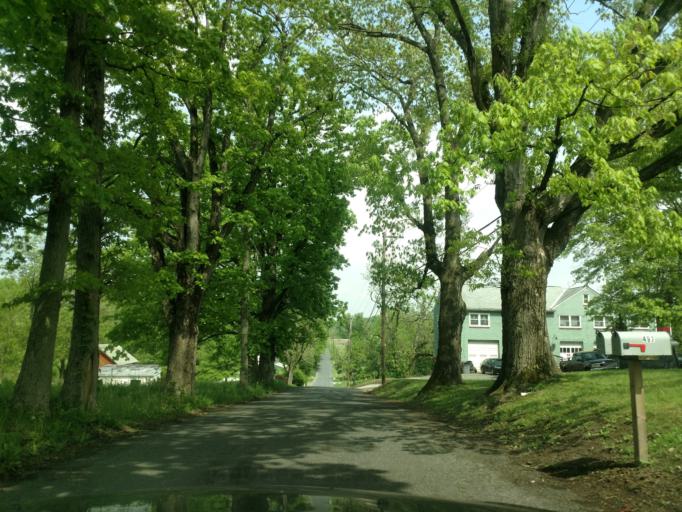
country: US
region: Pennsylvania
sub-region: Chester County
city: Spring City
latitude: 40.1466
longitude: -75.5488
